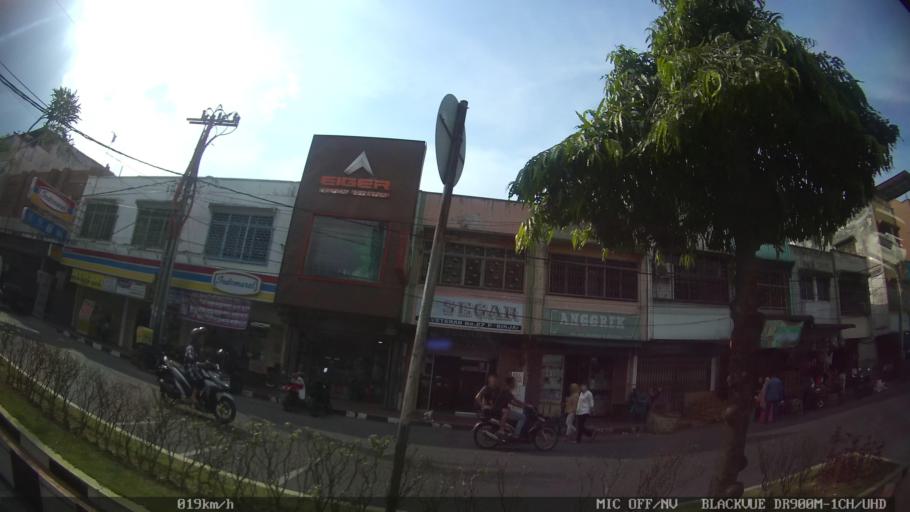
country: ID
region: North Sumatra
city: Binjai
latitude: 3.6054
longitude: 98.4866
